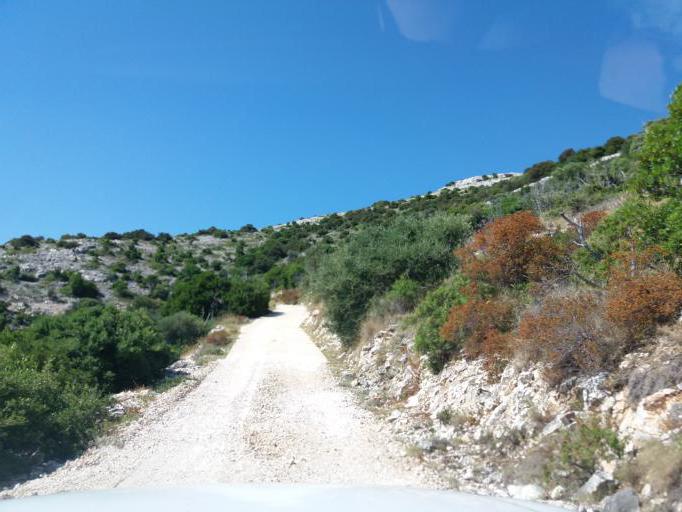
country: HR
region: Zadarska
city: Ugljan
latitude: 44.0088
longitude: 15.0344
